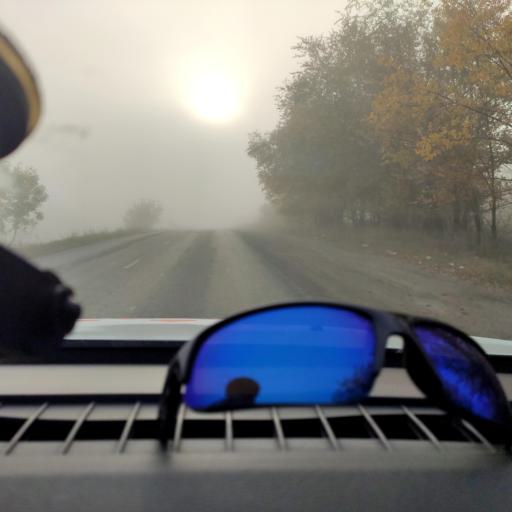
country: RU
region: Samara
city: Chapayevsk
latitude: 53.0053
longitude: 49.7444
